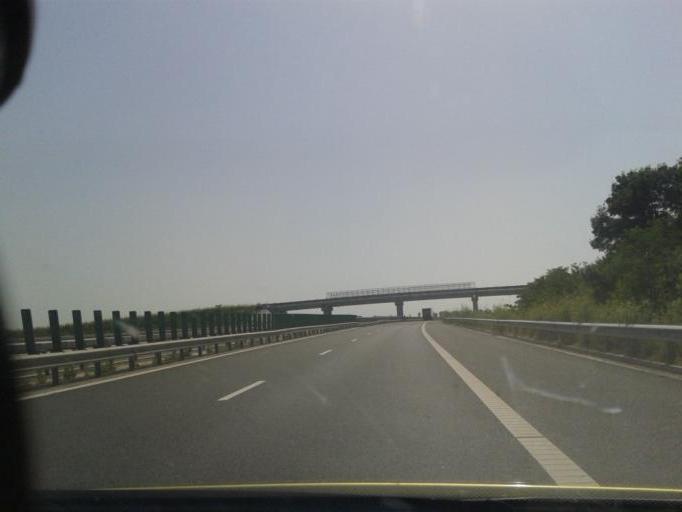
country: RO
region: Prahova
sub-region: Comuna Dumbrava
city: Dumbrava
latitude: 44.8621
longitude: 26.1819
